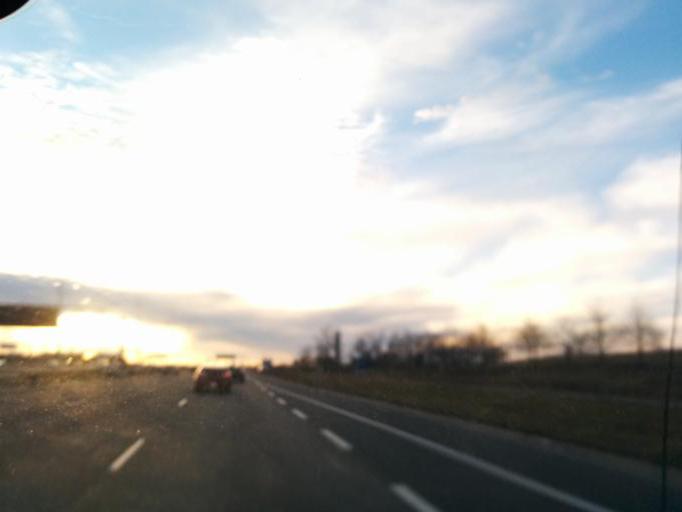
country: CA
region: Ontario
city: Etobicoke
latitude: 43.6679
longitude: -79.5948
